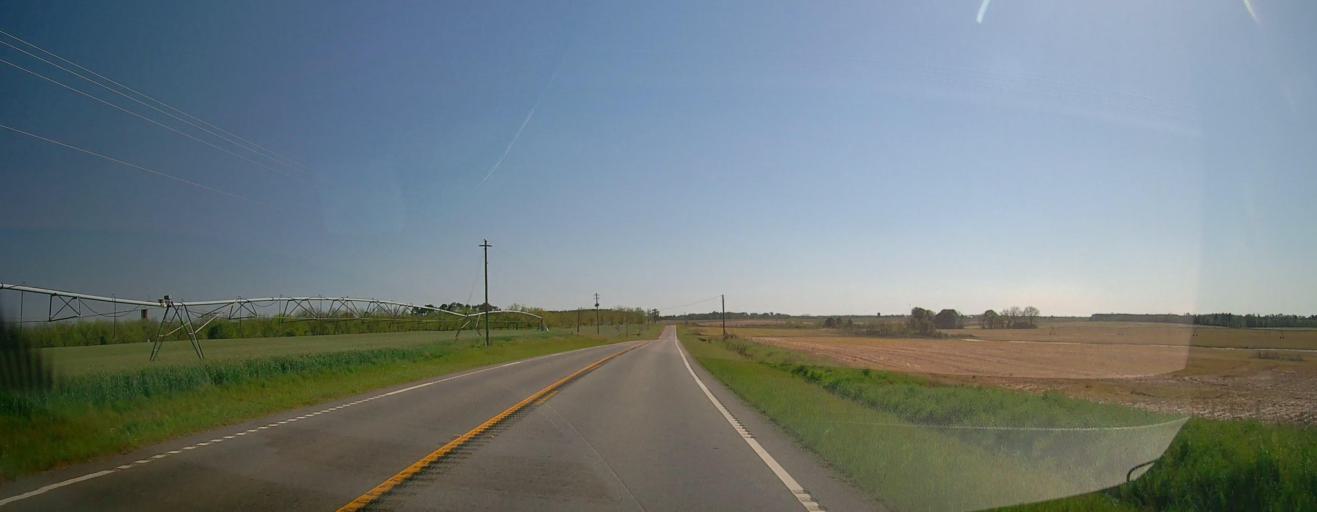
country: US
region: Georgia
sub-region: Pulaski County
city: Hawkinsville
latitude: 32.1791
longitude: -83.5062
